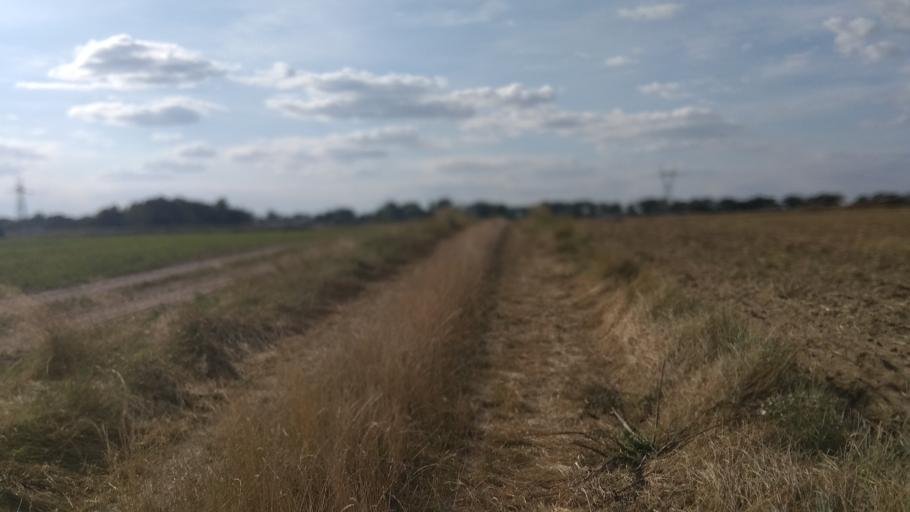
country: PL
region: Kujawsko-Pomorskie
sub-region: Powiat bydgoski
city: Osielsko
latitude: 53.2264
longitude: 18.1499
